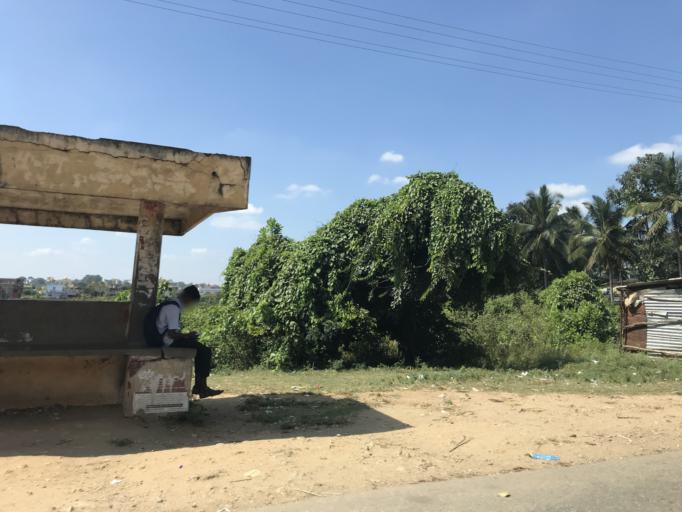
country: IN
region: Karnataka
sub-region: Mysore
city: Heggadadevankote
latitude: 12.0939
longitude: 76.3319
